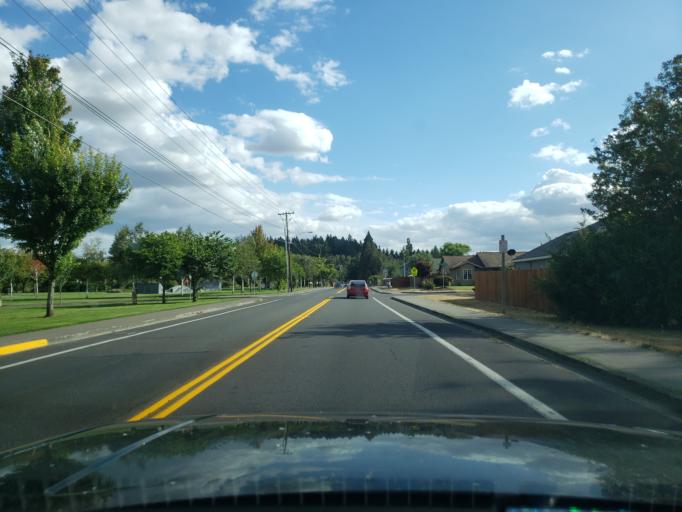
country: US
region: Oregon
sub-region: Yamhill County
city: McMinnville
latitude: 45.1990
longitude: -123.2191
